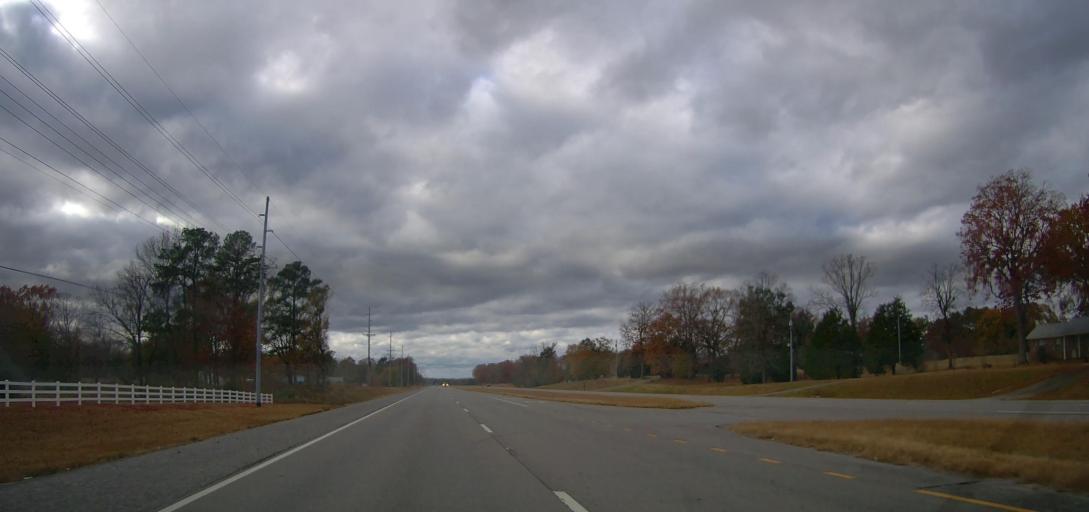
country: US
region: Alabama
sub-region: Lawrence County
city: Moulton
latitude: 34.5674
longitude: -87.3731
